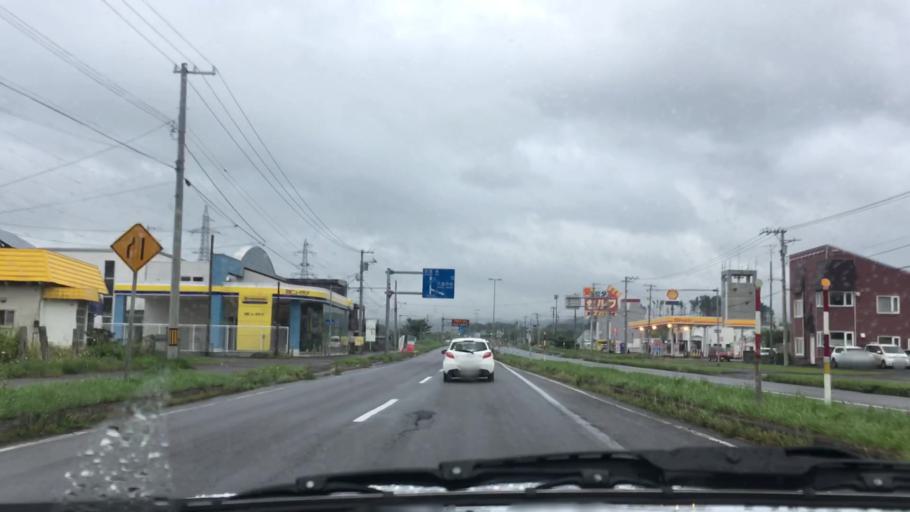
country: JP
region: Hokkaido
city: Nanae
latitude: 42.2487
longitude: 140.2872
